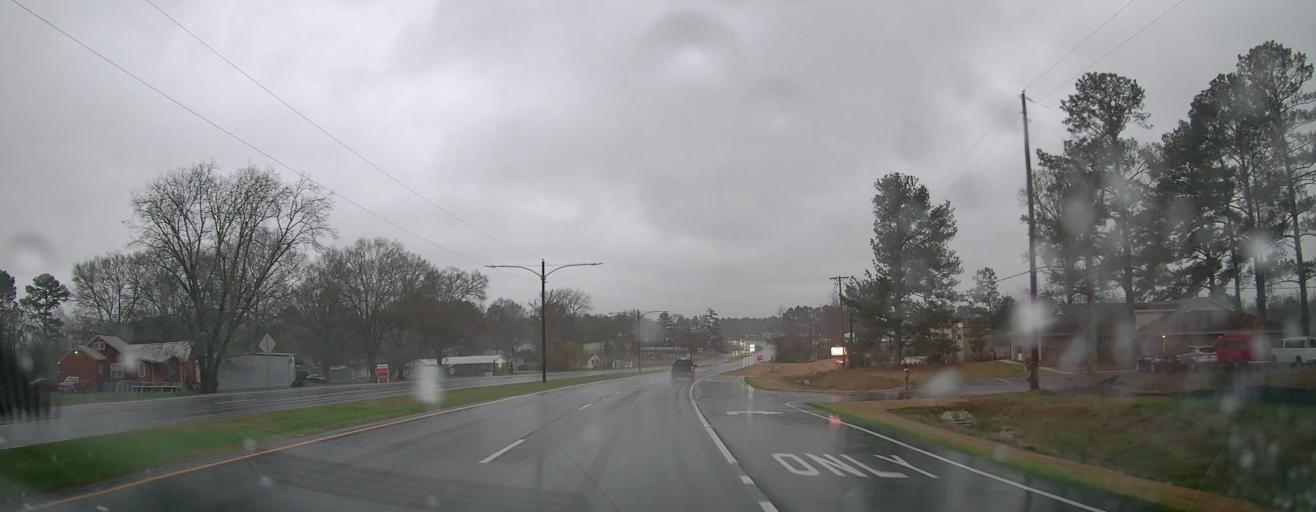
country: US
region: Alabama
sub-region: Morgan County
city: Hartselle
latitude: 34.4590
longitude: -86.9474
